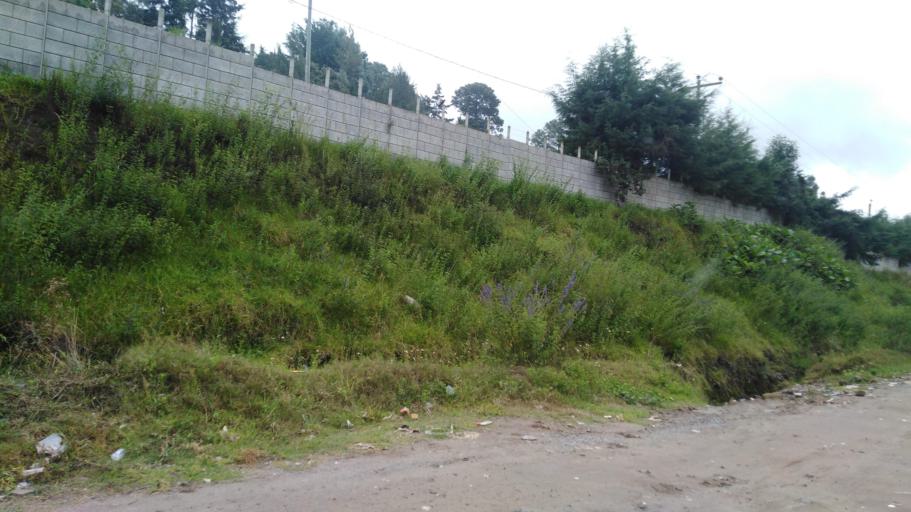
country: GT
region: Quetzaltenango
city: Quetzaltenango
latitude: 14.8561
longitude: -91.5054
